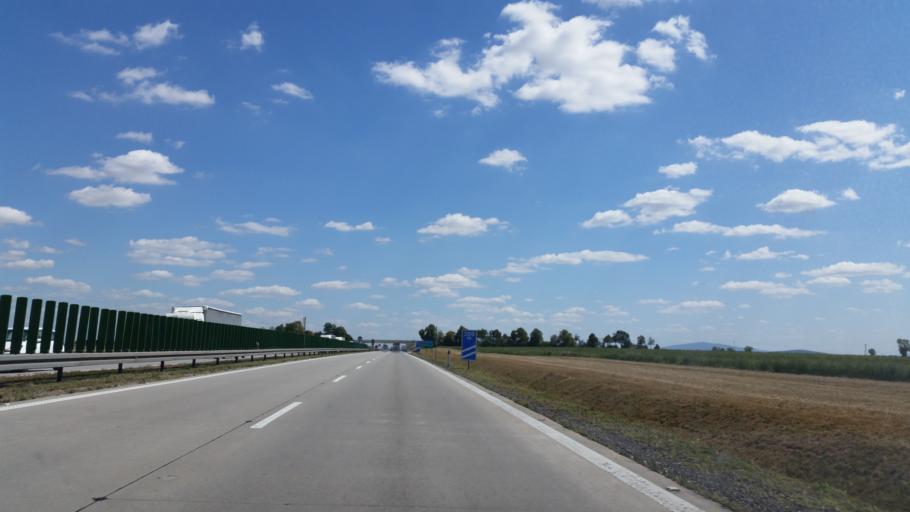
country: PL
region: Lower Silesian Voivodeship
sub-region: Powiat sredzki
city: Udanin
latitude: 51.0730
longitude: 16.4592
